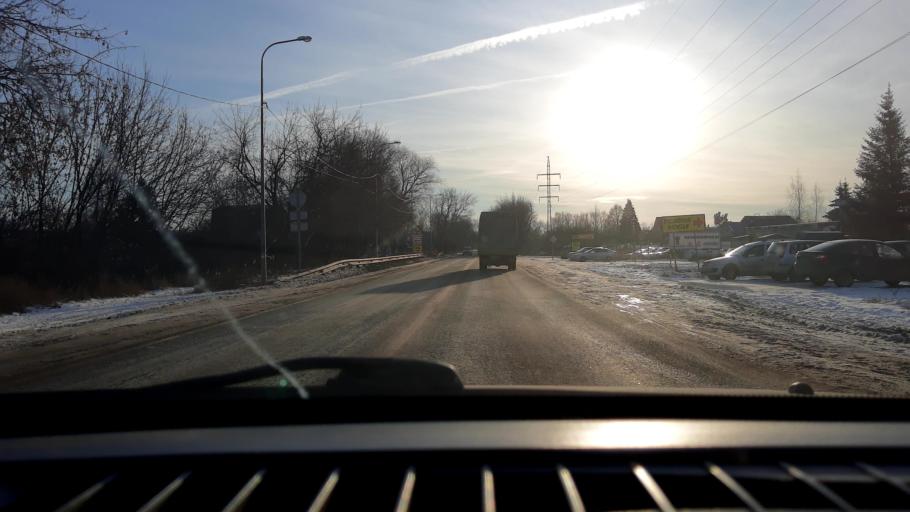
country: RU
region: Nizjnij Novgorod
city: Bor
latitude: 56.3698
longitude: 44.0670
